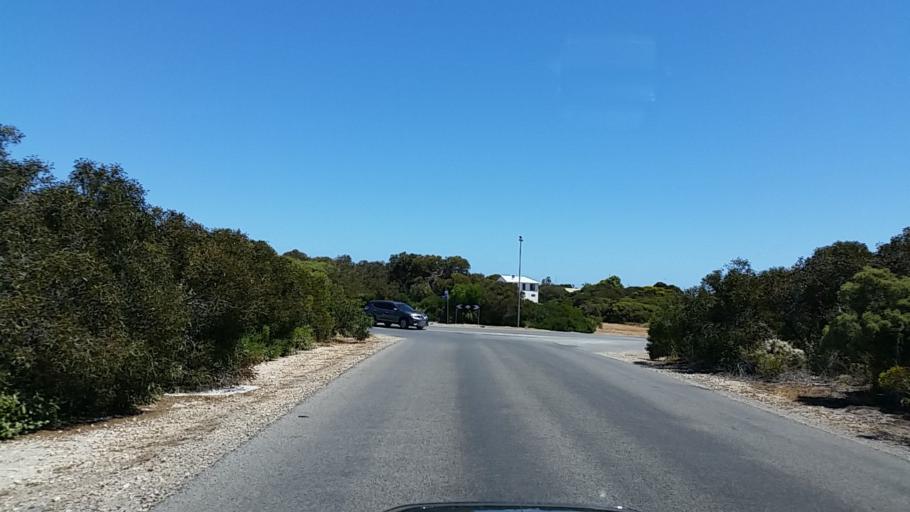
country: AU
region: South Australia
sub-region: Yorke Peninsula
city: Honiton
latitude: -35.2439
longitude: 136.9760
